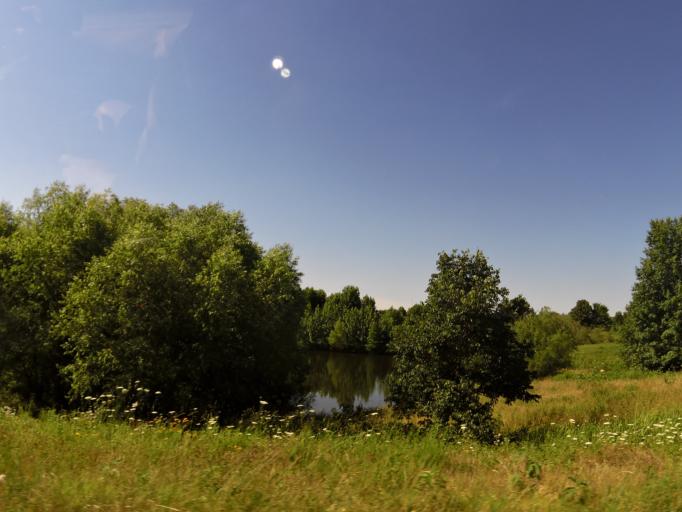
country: US
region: Arkansas
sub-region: Clay County
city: Piggott
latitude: 36.4336
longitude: -90.3175
